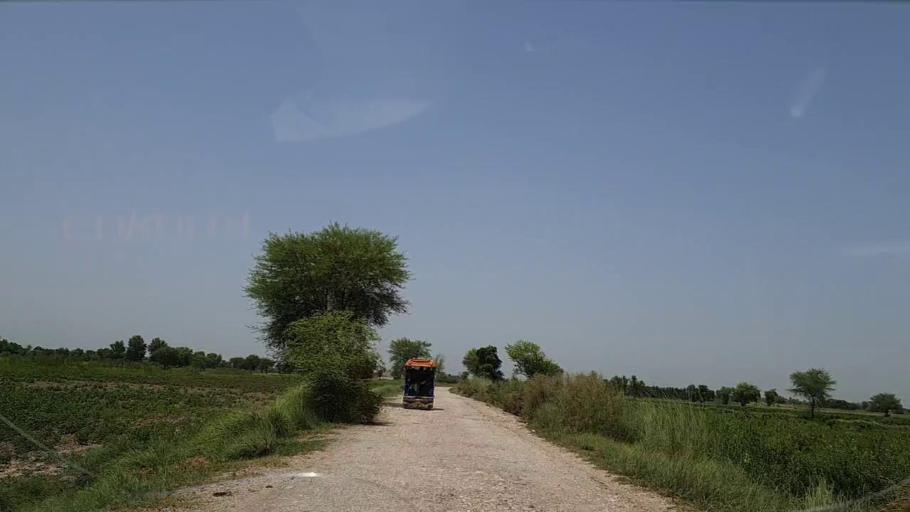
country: PK
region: Sindh
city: Tharu Shah
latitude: 26.9290
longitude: 68.0516
